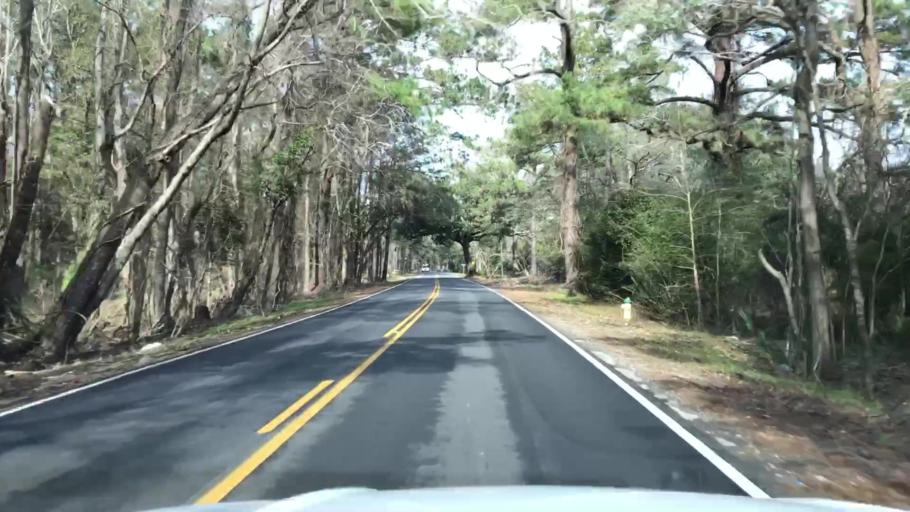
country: US
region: South Carolina
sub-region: Charleston County
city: Folly Beach
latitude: 32.7133
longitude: -80.0188
